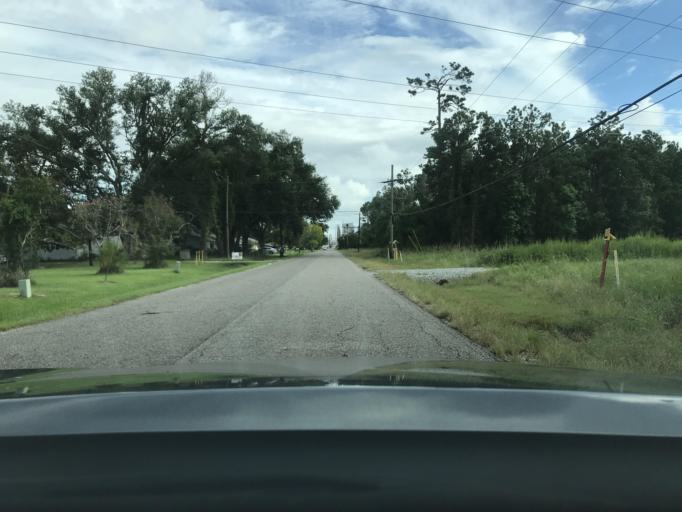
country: US
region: Louisiana
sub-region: Calcasieu Parish
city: Westlake
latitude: 30.2602
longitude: -93.2751
